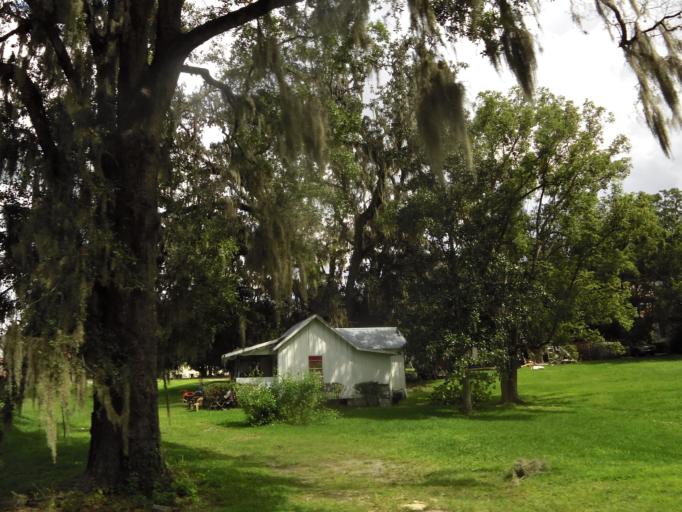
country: US
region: Florida
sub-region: Union County
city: Lake Butler
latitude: 30.0222
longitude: -82.3390
